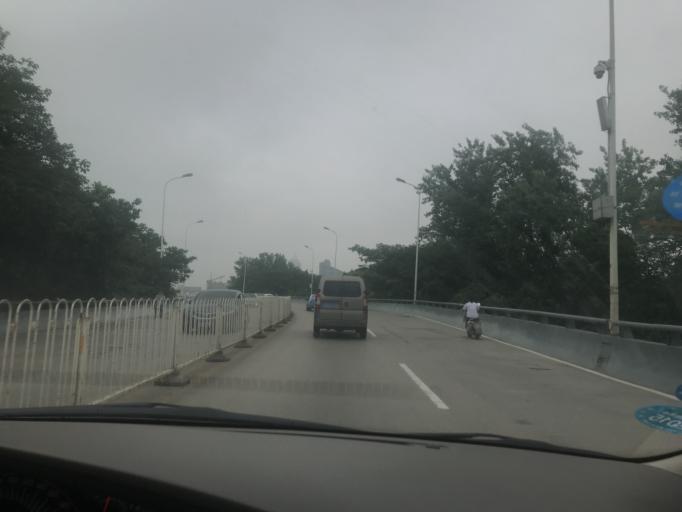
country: CN
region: Hubei
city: Wuhan
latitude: 30.5632
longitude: 114.2804
